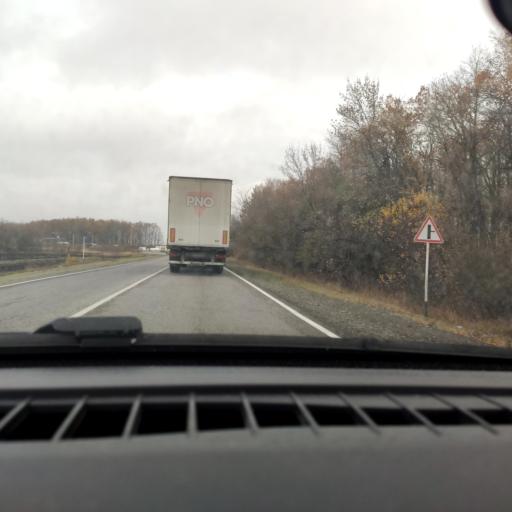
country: RU
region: Voronezj
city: Shilovo
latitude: 51.4251
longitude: 39.0083
